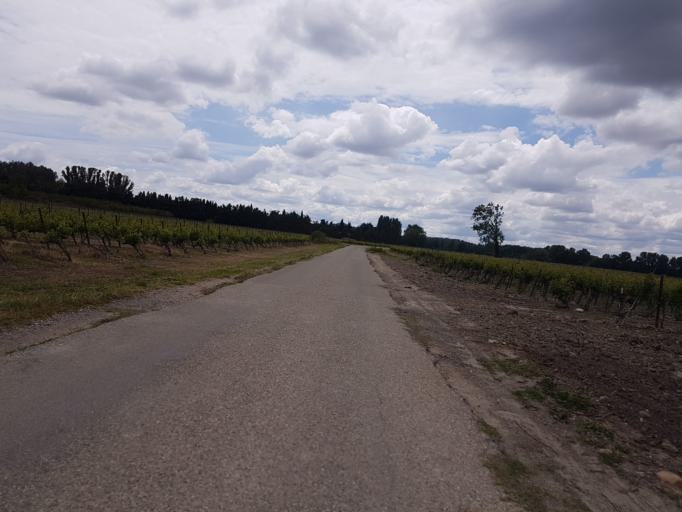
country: FR
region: Languedoc-Roussillon
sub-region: Departement du Gard
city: Vallabregues
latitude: 43.8742
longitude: 4.6250
